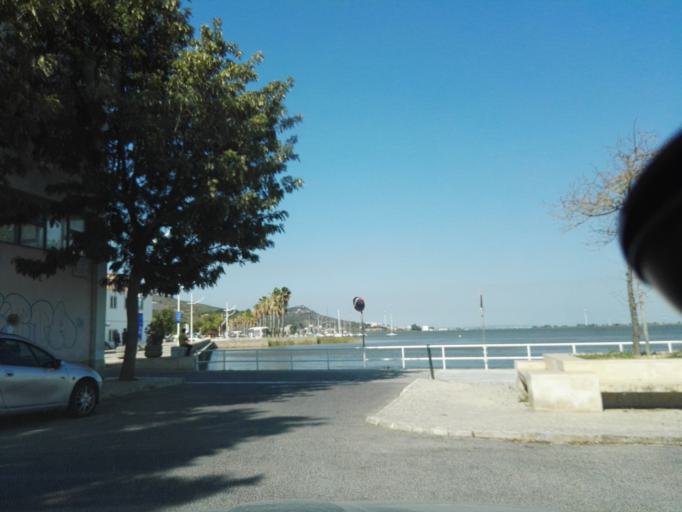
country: PT
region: Lisbon
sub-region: Vila Franca de Xira
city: Alhandra
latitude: 38.9253
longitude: -9.0062
